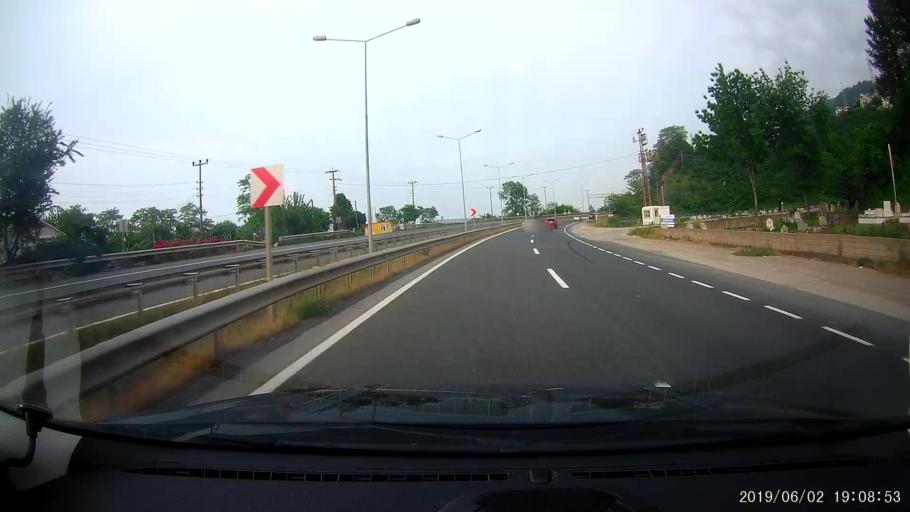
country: TR
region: Ordu
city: Gulyali
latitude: 40.9763
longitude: 38.0183
